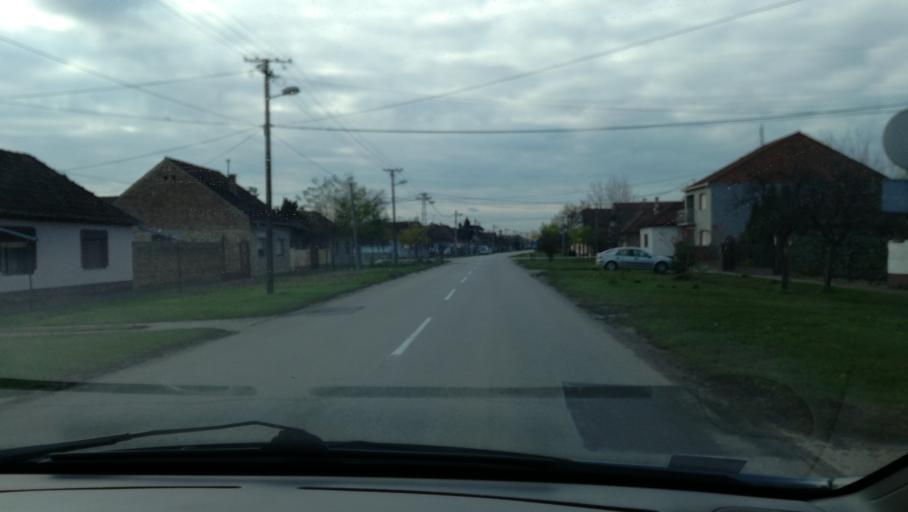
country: RS
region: Autonomna Pokrajina Vojvodina
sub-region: Severnobanatski Okrug
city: Kikinda
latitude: 45.8314
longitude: 20.4424
